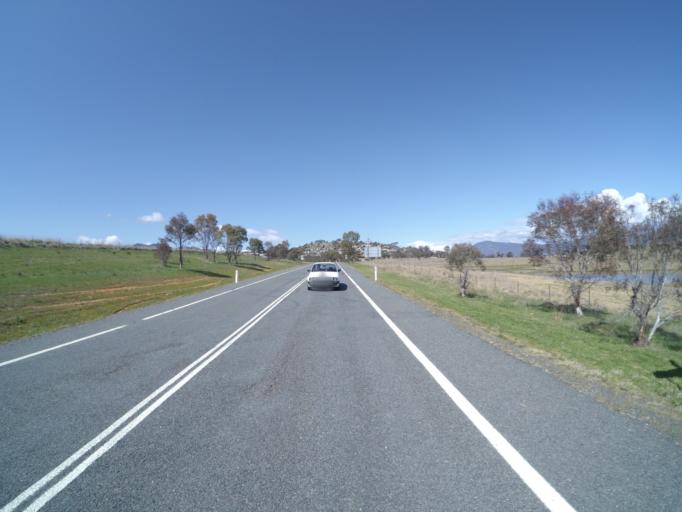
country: AU
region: Australian Capital Territory
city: Macarthur
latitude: -35.4540
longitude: 149.0757
